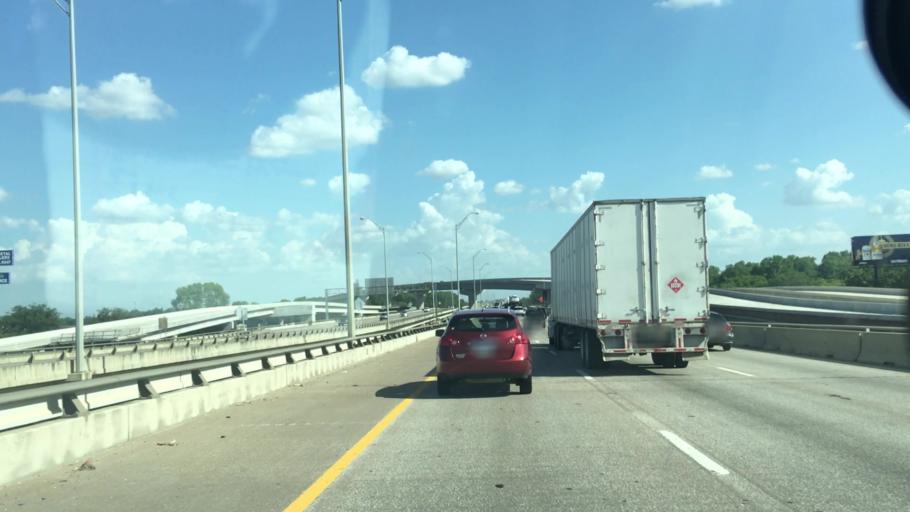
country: US
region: Texas
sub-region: Dallas County
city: Dallas
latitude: 32.7505
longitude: -96.7703
